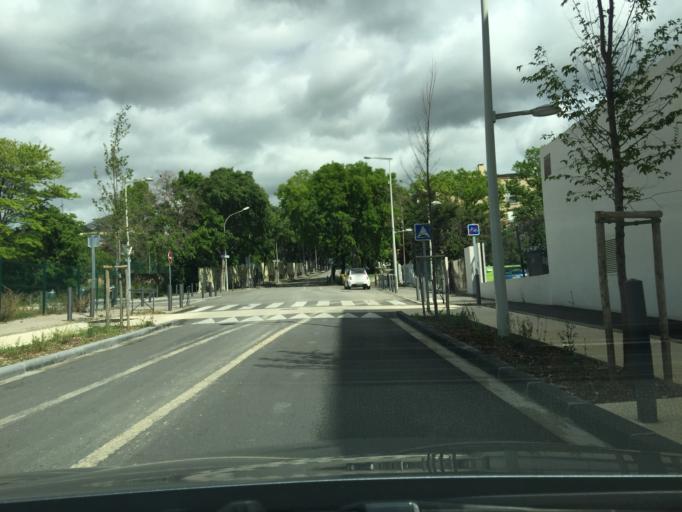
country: FR
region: Provence-Alpes-Cote d'Azur
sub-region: Departement des Bouches-du-Rhone
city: Marseille 10
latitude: 43.2638
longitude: 5.4196
